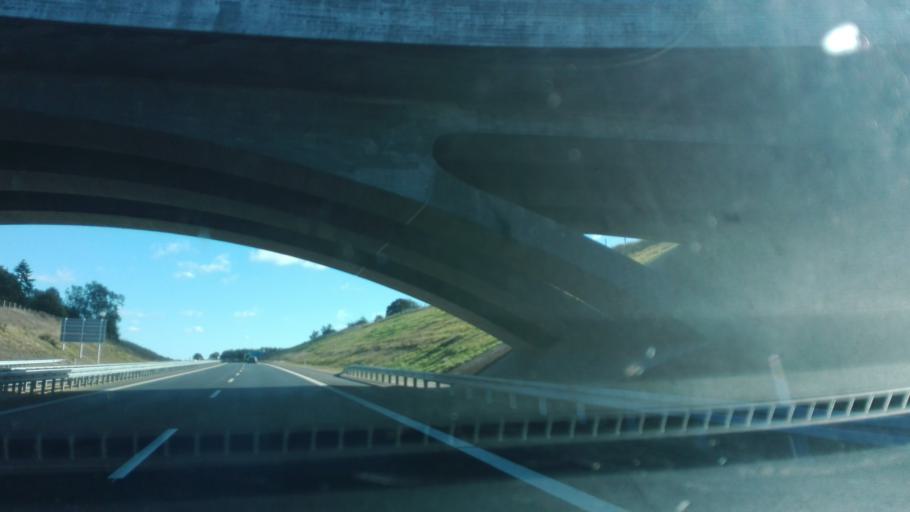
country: DK
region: Central Jutland
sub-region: Silkeborg Kommune
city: Svejbaek
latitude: 56.1570
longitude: 9.6220
